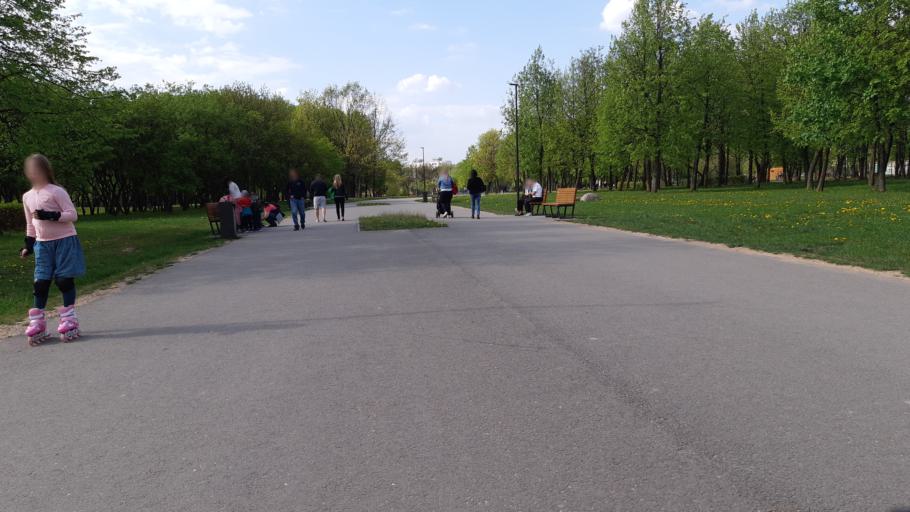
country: LT
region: Kauno apskritis
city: Dainava (Kaunas)
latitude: 54.9222
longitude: 23.9526
